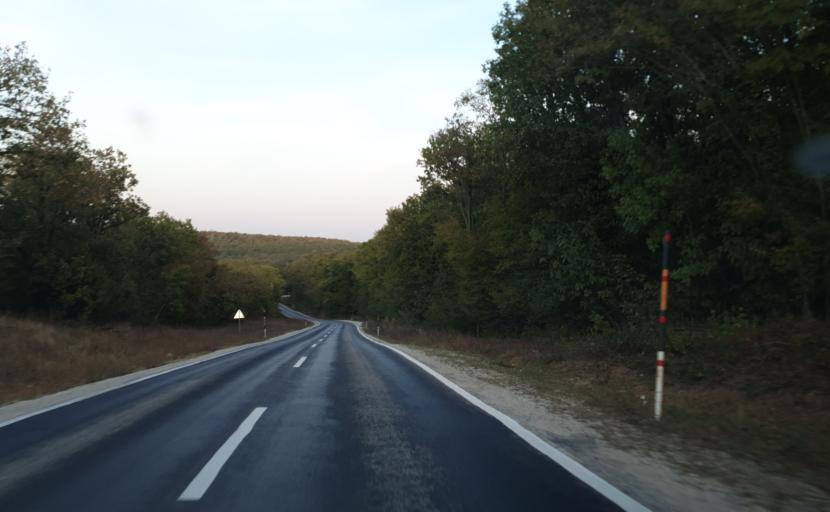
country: TR
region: Kirklareli
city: Igneada
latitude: 41.8795
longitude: 27.8953
